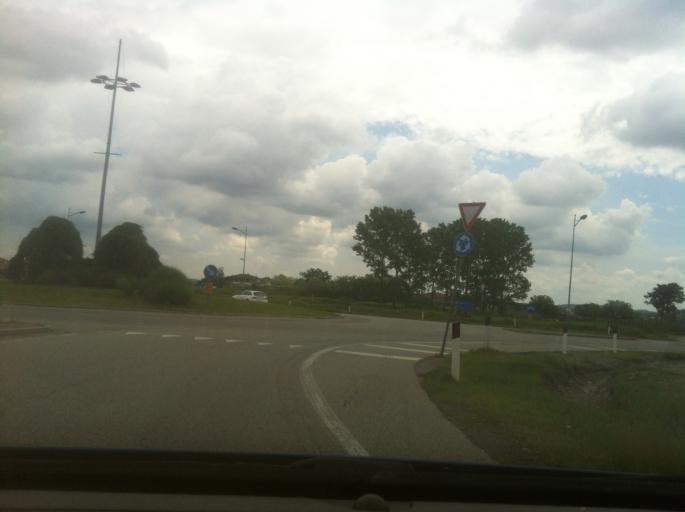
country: IT
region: Piedmont
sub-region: Provincia di Torino
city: Romano Canavese
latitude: 45.3861
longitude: 7.8623
